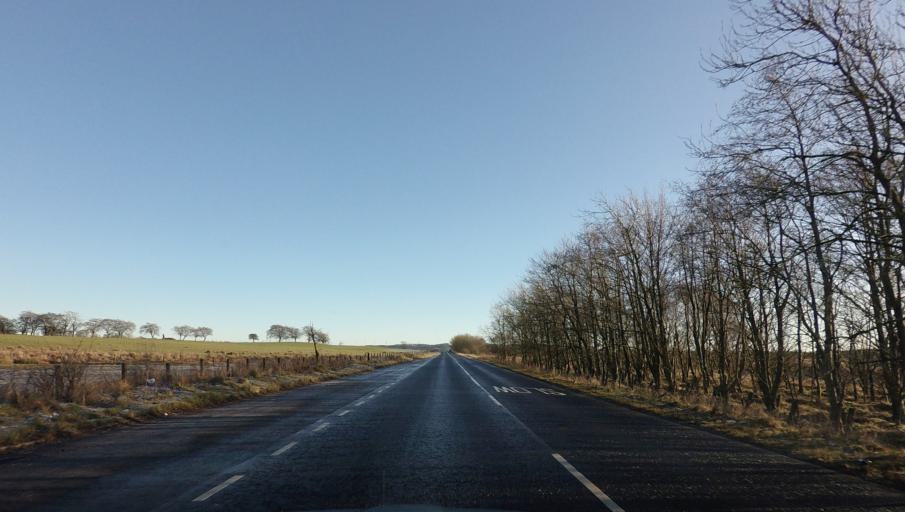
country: GB
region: Scotland
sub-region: North Lanarkshire
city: Shotts
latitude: 55.8056
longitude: -3.7714
